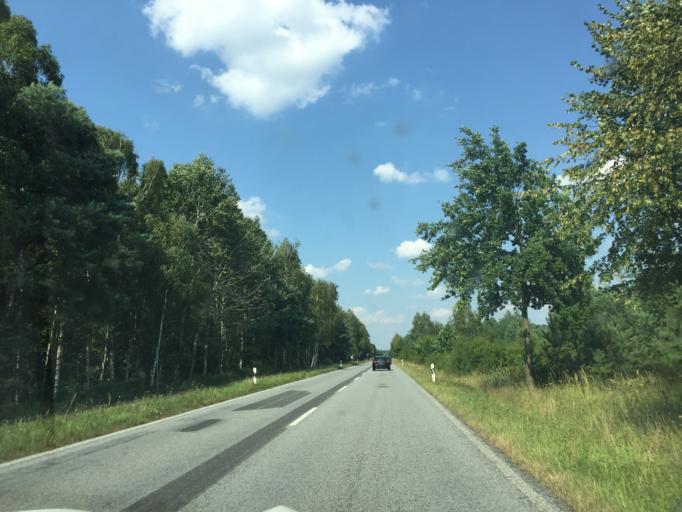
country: DE
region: Saxony
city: Schleife
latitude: 51.4668
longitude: 14.4937
